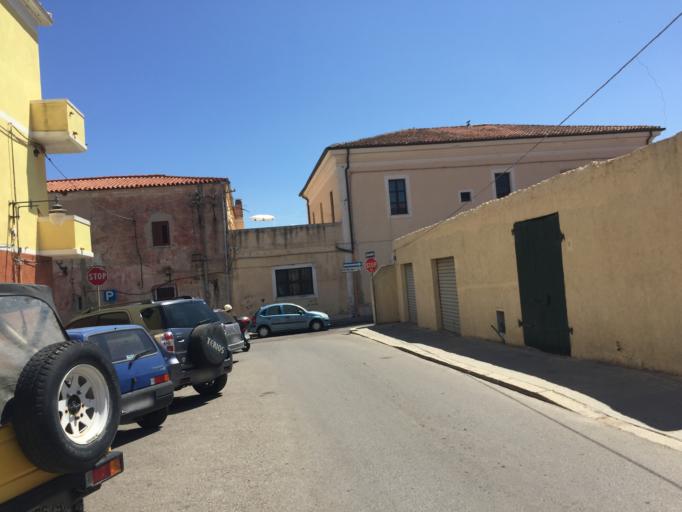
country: IT
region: Sardinia
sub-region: Provincia di Olbia-Tempio
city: La Maddalena
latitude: 41.2154
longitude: 9.4071
